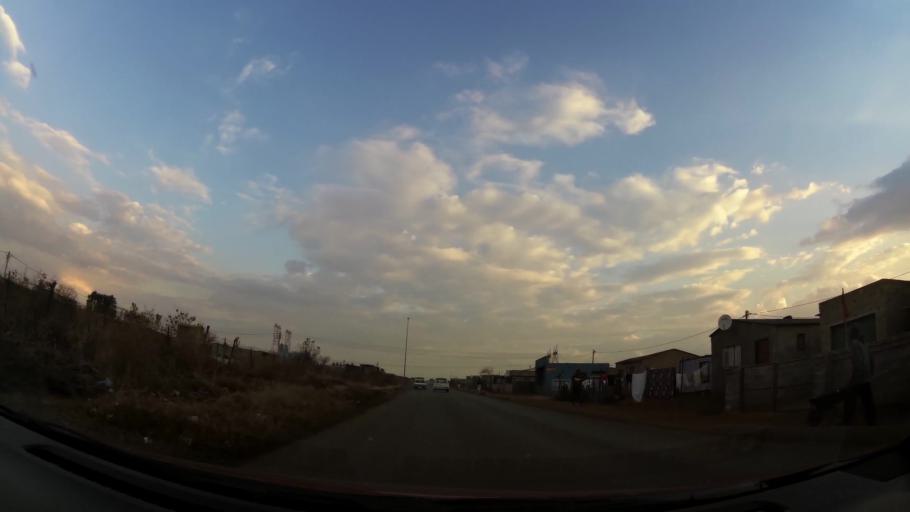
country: ZA
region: Gauteng
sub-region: City of Johannesburg Metropolitan Municipality
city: Orange Farm
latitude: -26.5536
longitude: 27.8398
